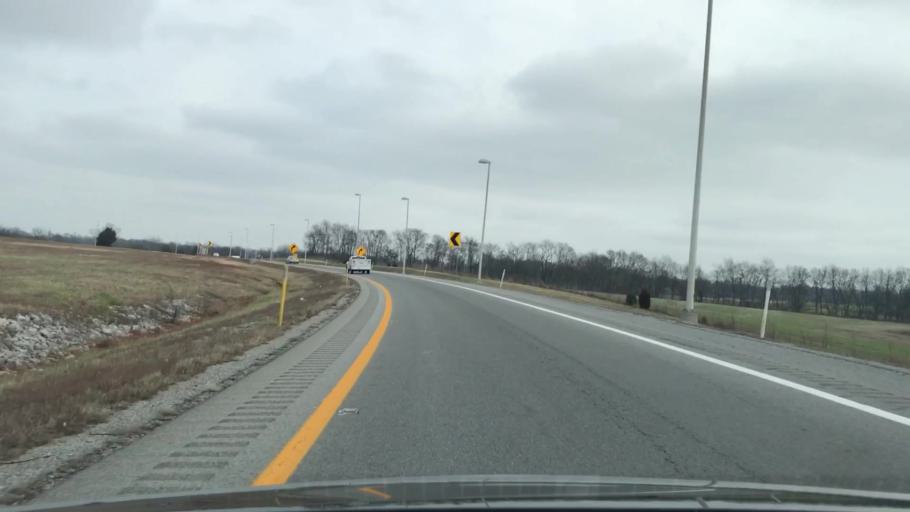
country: US
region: Kentucky
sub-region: Christian County
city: Fort Campbell North
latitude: 36.7389
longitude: -87.5061
